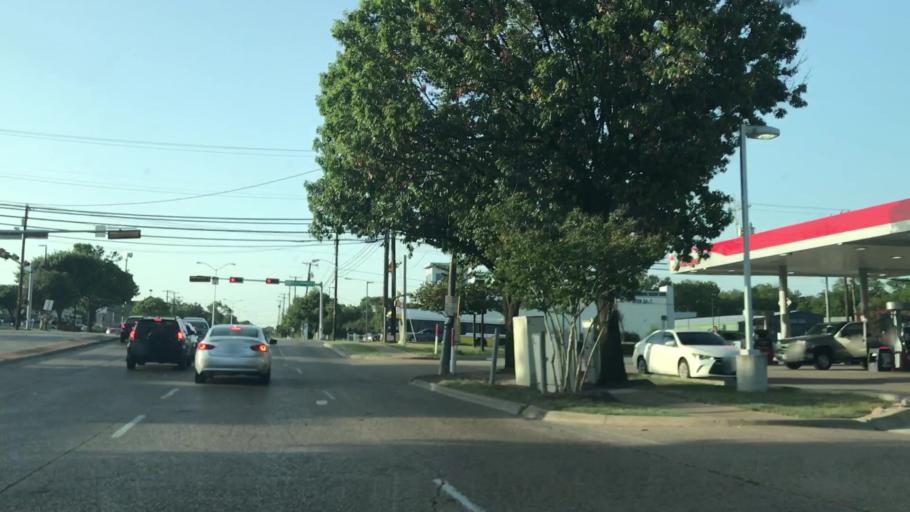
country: US
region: Texas
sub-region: Dallas County
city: Garland
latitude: 32.8636
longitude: -96.7004
